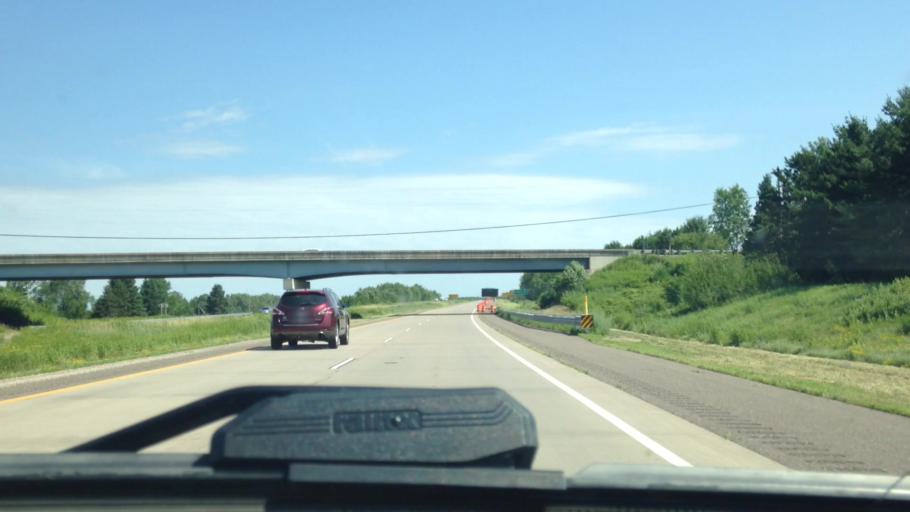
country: US
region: Wisconsin
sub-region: Barron County
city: Rice Lake
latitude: 45.5661
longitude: -91.7646
